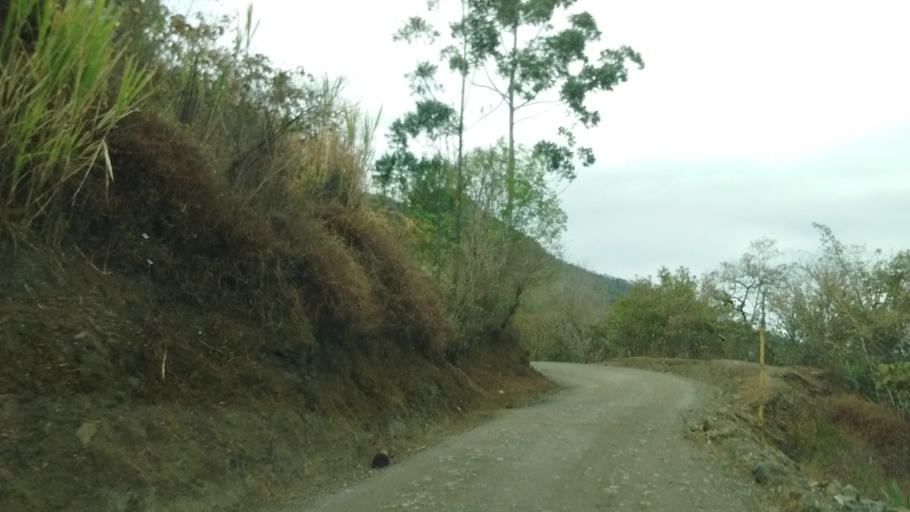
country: CO
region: Cauca
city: Almaguer
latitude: 1.8626
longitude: -76.9330
